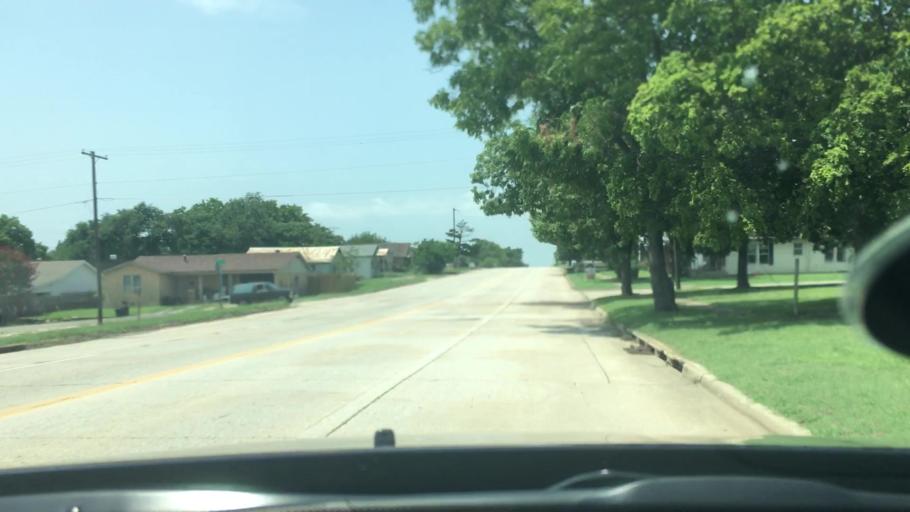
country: US
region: Oklahoma
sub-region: Murray County
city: Sulphur
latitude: 34.5109
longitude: -96.9595
